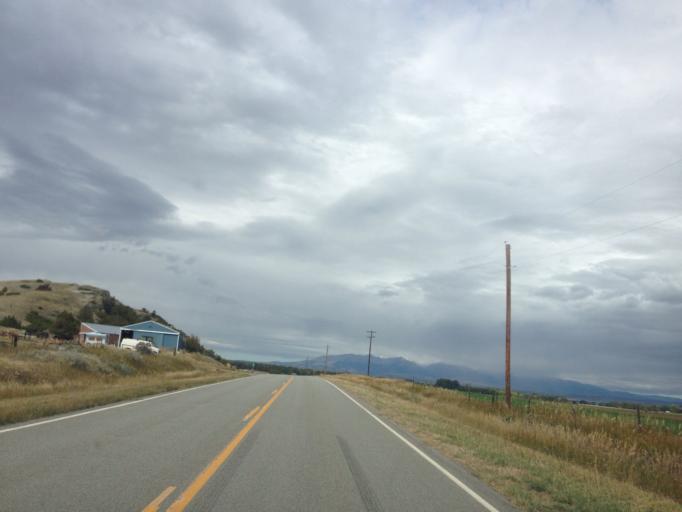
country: US
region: Montana
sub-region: Sweet Grass County
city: Big Timber
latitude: 45.7793
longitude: -109.8154
